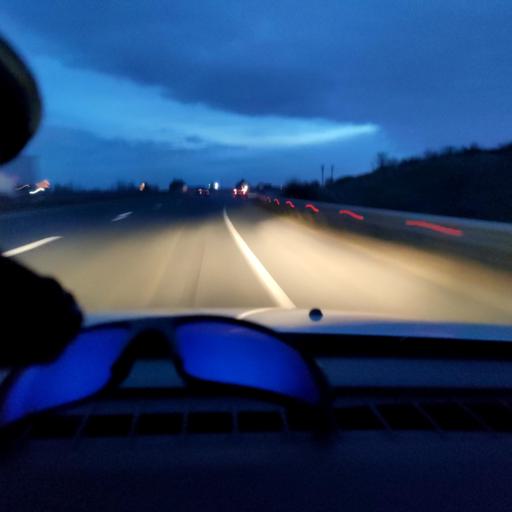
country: RU
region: Samara
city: Novokuybyshevsk
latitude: 53.0609
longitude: 50.0196
